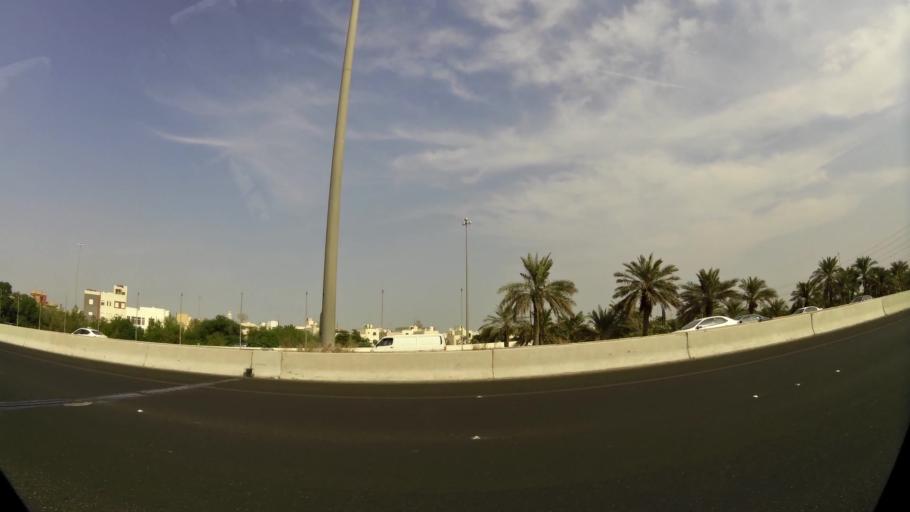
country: KW
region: Al Farwaniyah
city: Al Farwaniyah
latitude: 29.3054
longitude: 47.9785
